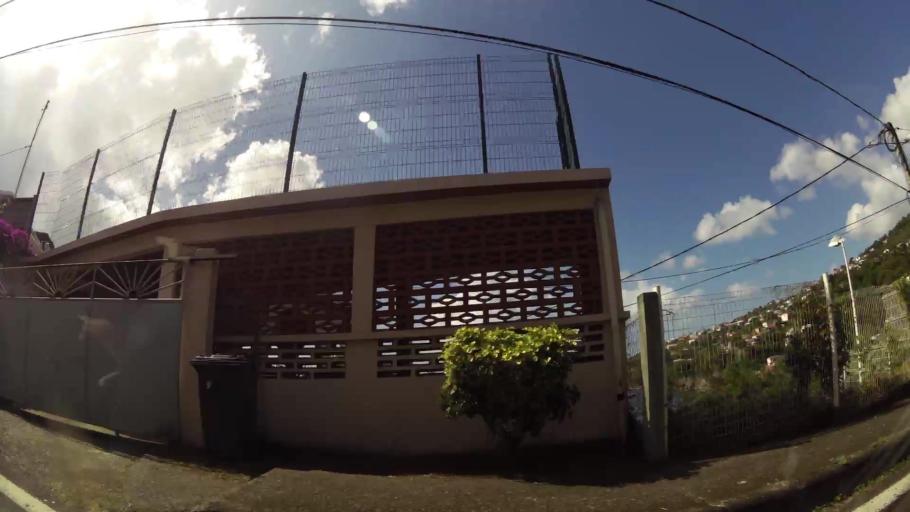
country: MQ
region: Martinique
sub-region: Martinique
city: Fort-de-France
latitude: 14.6249
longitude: -61.1106
